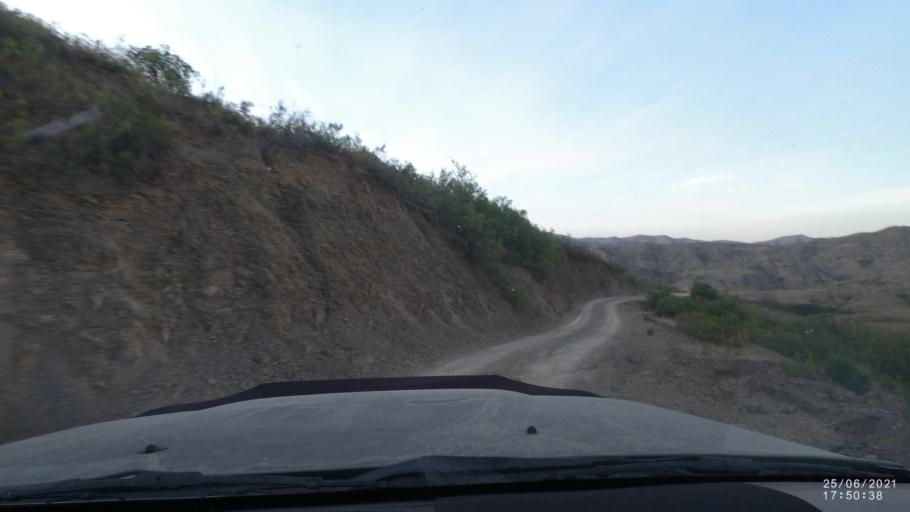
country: BO
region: Cochabamba
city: Mizque
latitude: -17.9528
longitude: -65.6412
